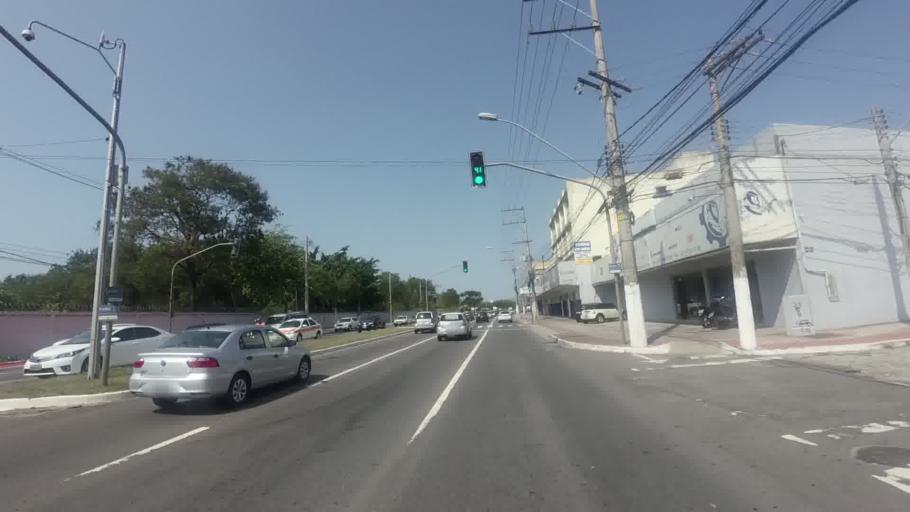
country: BR
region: Espirito Santo
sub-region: Vila Velha
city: Vila Velha
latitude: -20.2599
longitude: -40.2926
